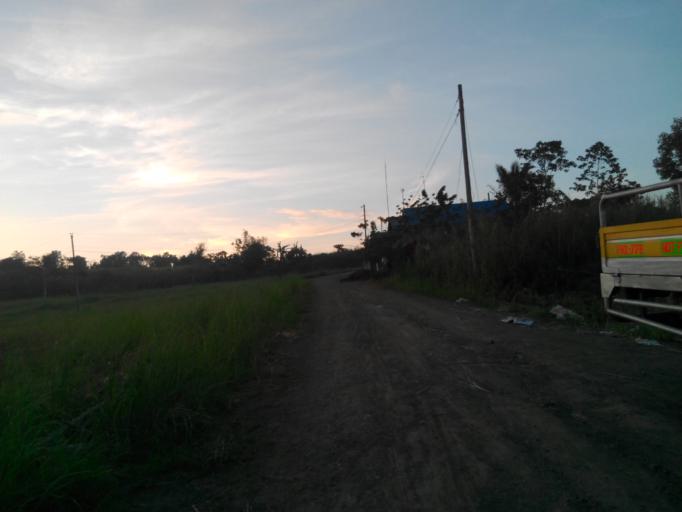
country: PH
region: Western Visayas
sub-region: Province of Iloilo
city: Passi
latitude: 11.1220
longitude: 122.6475
